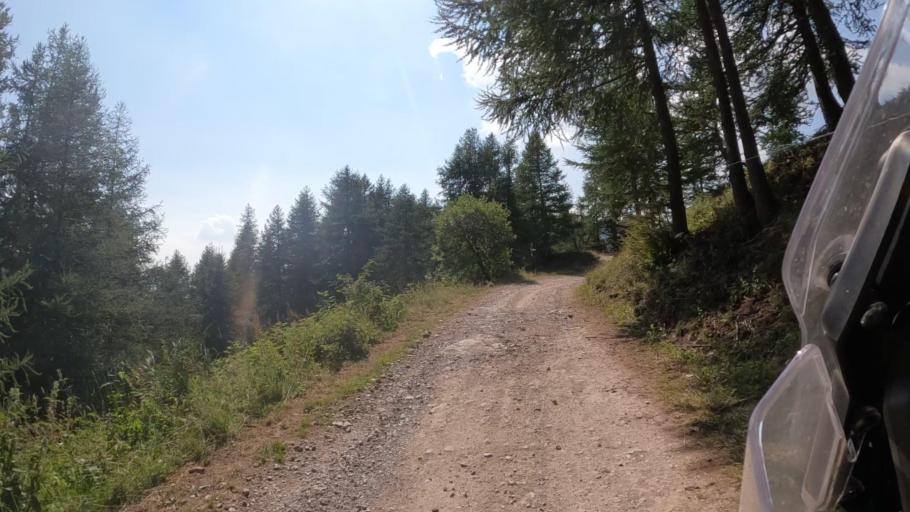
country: IT
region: Piedmont
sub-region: Provincia di Cuneo
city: Briga Alta
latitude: 44.0839
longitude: 7.7325
